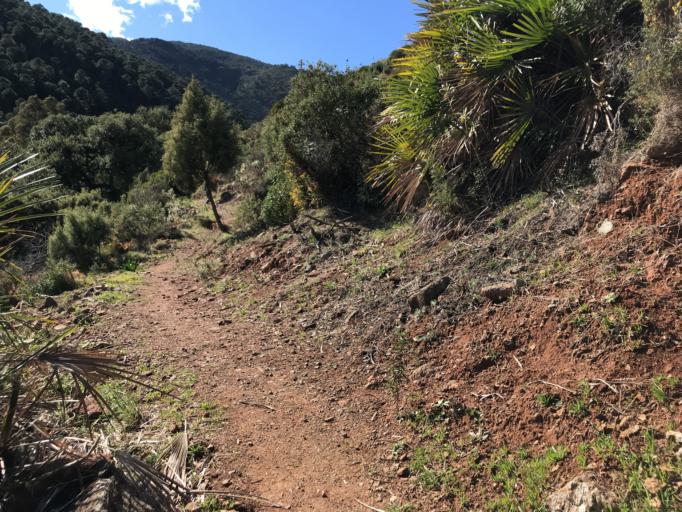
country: ES
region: Andalusia
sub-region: Provincia de Malaga
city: Tolox
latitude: 36.6720
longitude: -4.9213
